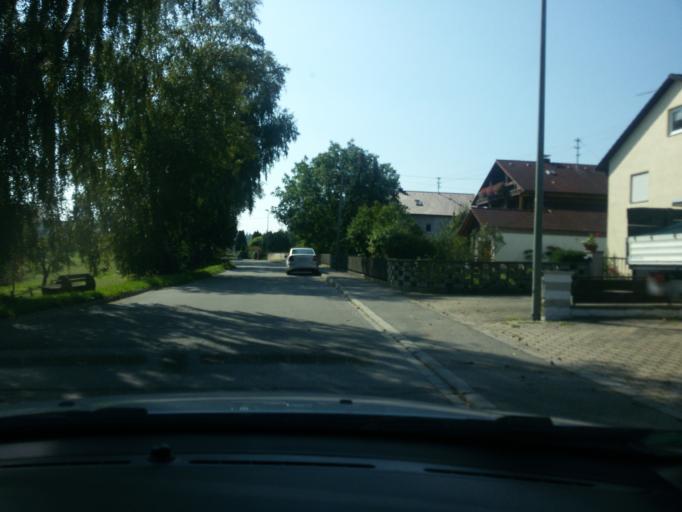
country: DE
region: Bavaria
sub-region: Swabia
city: Hiltenfingen
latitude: 48.1856
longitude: 10.6815
